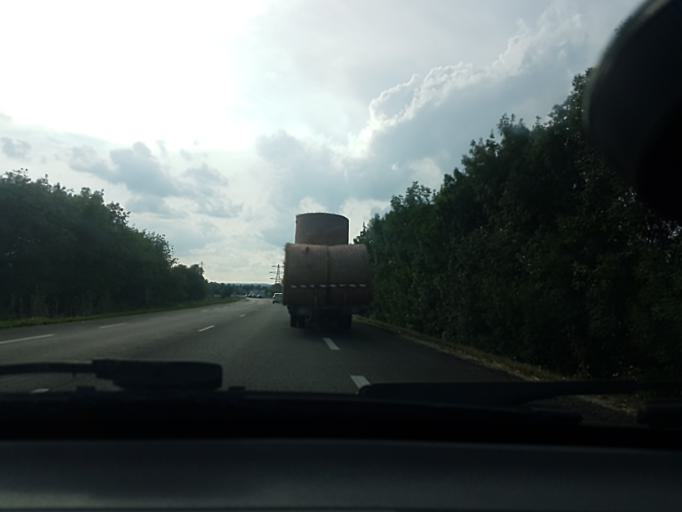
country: FR
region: Bourgogne
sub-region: Departement de Saone-et-Loire
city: Saint-Remy
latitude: 46.7582
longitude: 4.8508
